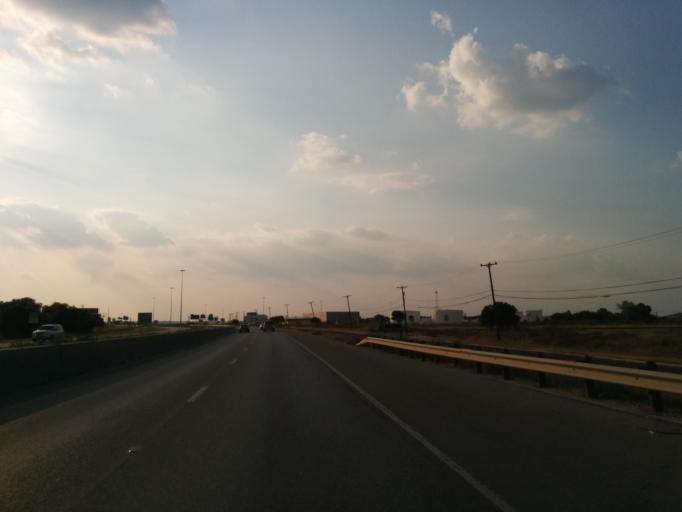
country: US
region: Texas
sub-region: Bexar County
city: Kirby
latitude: 29.4441
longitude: -98.3962
